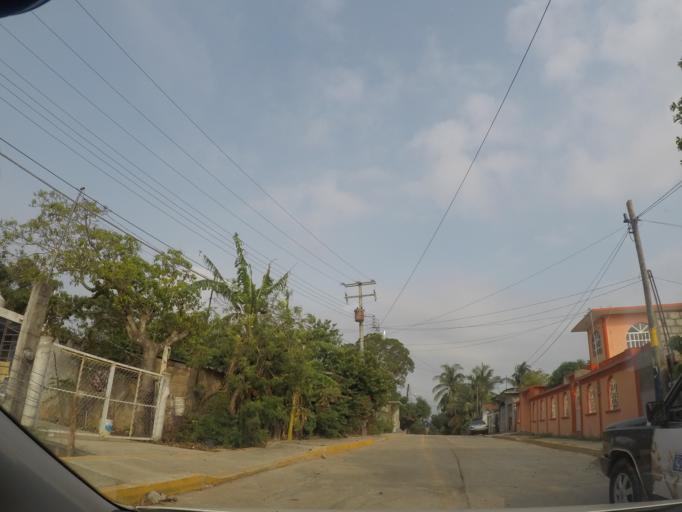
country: MX
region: Oaxaca
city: Colonia Rincon Viejo
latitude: 16.8870
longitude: -95.0459
